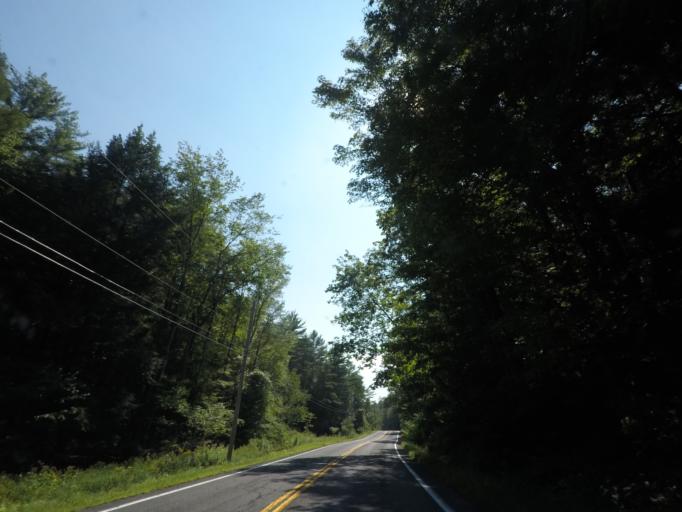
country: US
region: New York
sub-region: Rensselaer County
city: Hoosick Falls
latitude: 42.8333
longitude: -73.4742
